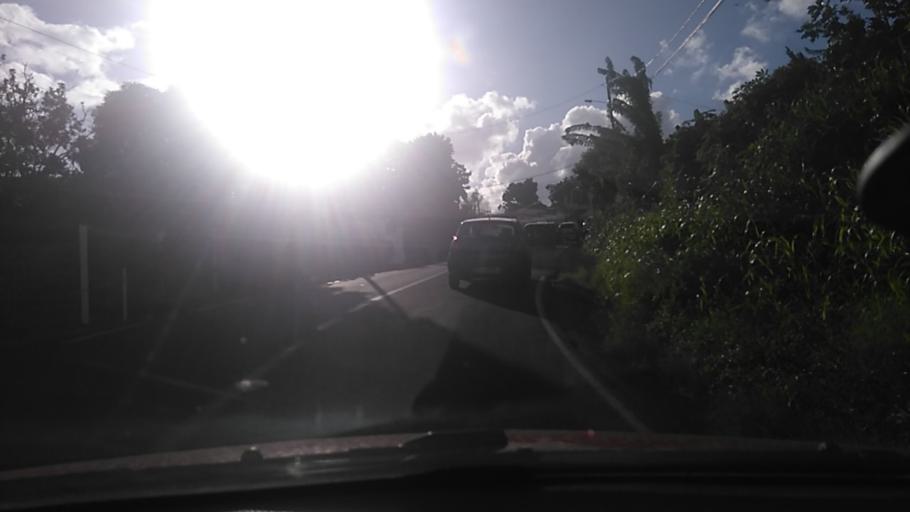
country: MQ
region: Martinique
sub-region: Martinique
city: Ducos
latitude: 14.5721
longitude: -60.9639
